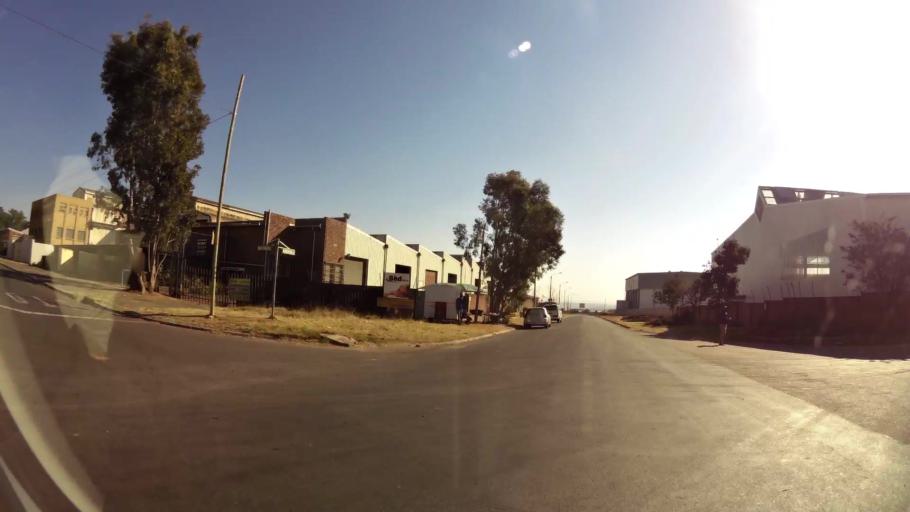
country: ZA
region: Gauteng
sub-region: City of Johannesburg Metropolitan Municipality
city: Modderfontein
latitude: -26.0658
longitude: 28.1907
